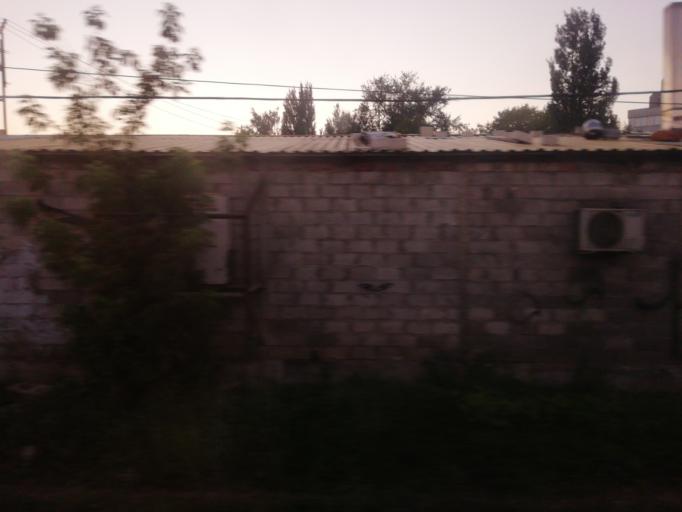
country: RU
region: Moscow
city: Mar'ina Roshcha
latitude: 55.7974
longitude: 37.5937
